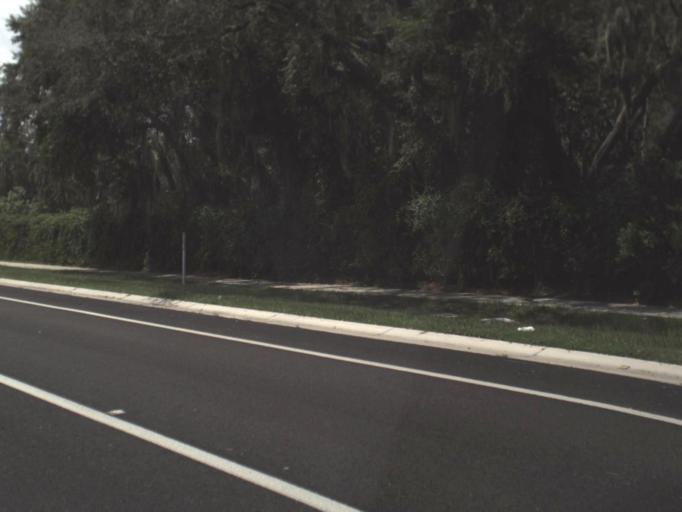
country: US
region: Florida
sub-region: Hillsborough County
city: Riverview
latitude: 27.8469
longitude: -82.3269
